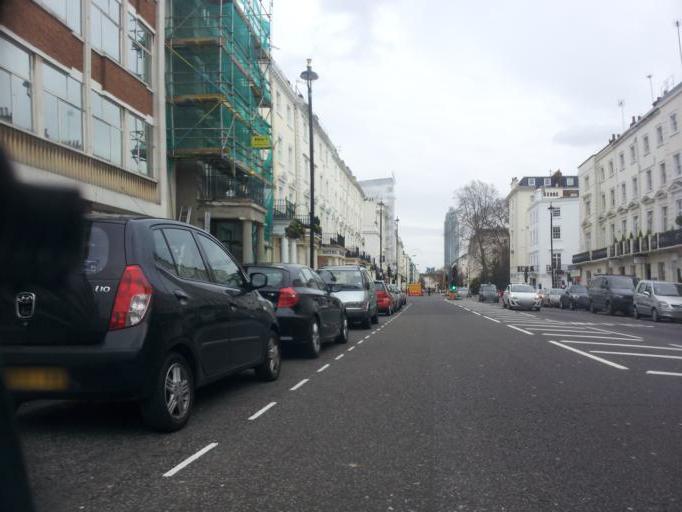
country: GB
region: England
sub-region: Greater London
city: Battersea
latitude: 51.4923
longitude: -0.1420
